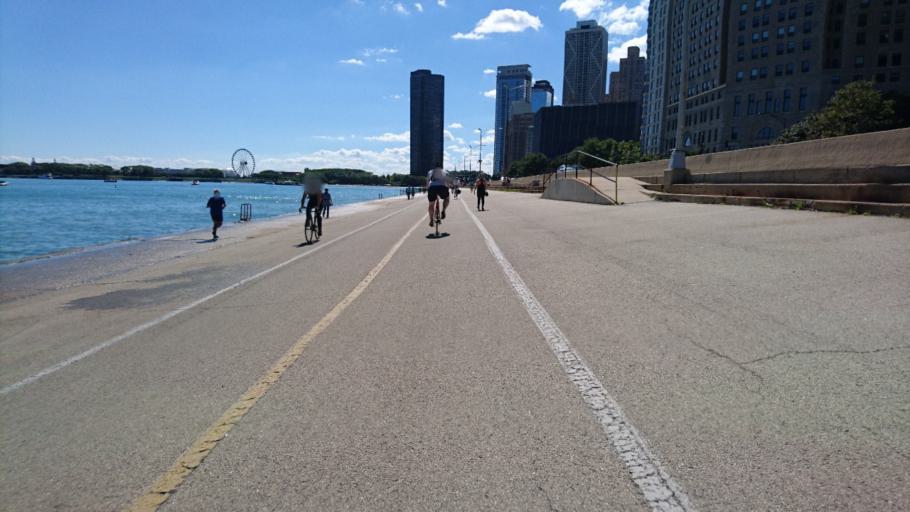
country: US
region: Illinois
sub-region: Cook County
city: Chicago
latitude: 41.8995
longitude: -87.6184
